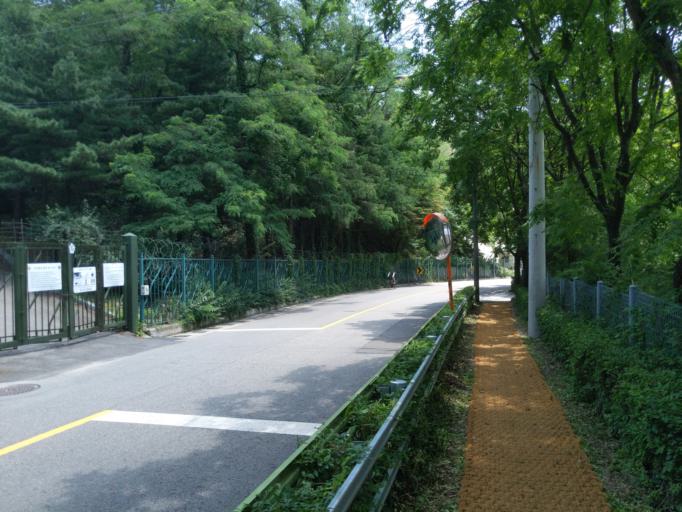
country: KR
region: Seoul
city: Seoul
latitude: 37.5982
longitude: 126.9739
